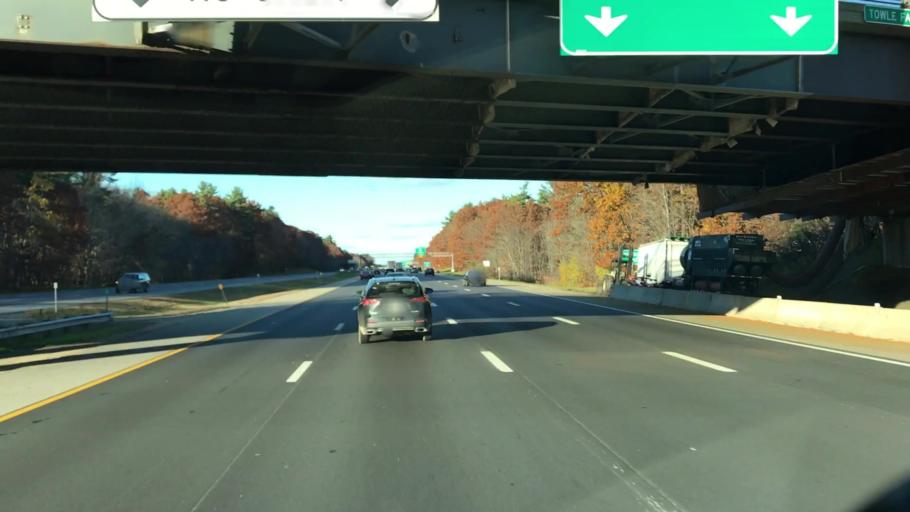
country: US
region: New Hampshire
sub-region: Rockingham County
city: Hampton
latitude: 42.9425
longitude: -70.8602
